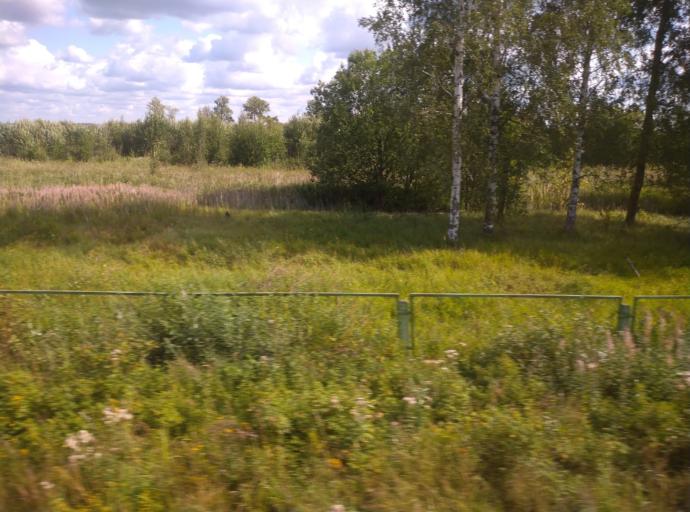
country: RU
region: St.-Petersburg
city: Sapernyy
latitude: 59.7325
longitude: 30.6359
